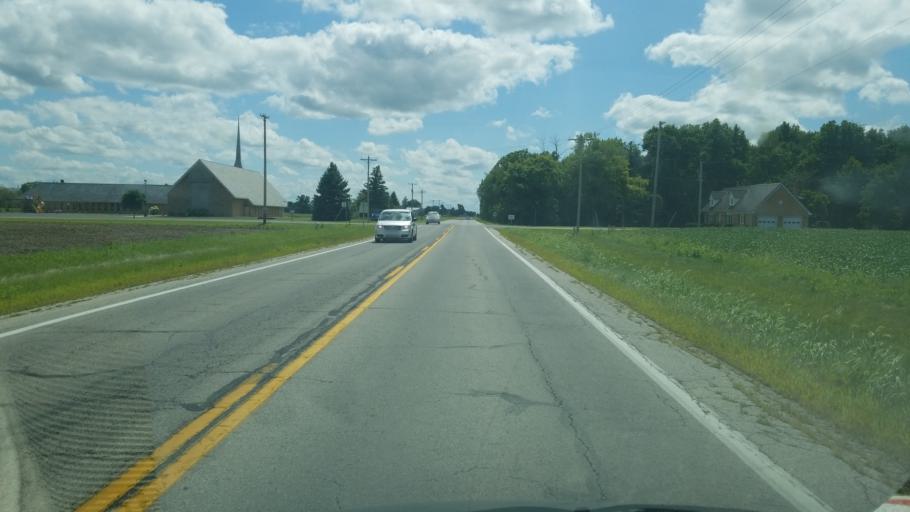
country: US
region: Ohio
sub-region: Henry County
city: Holgate
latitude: 41.2982
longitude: -84.1176
